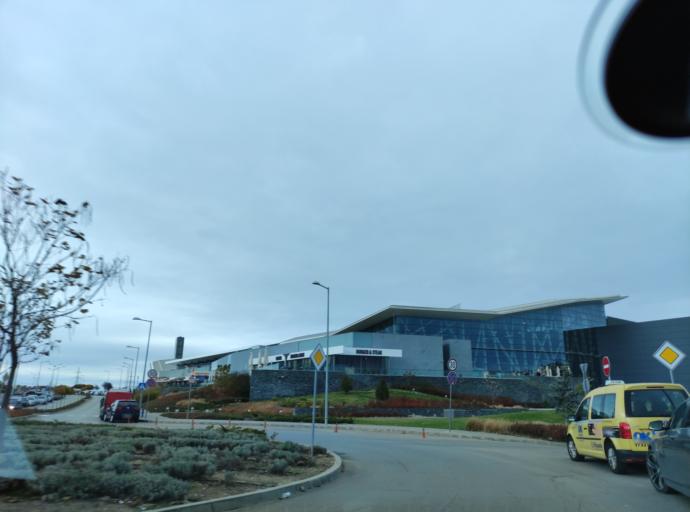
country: BG
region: Sofia-Capital
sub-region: Stolichna Obshtina
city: Sofia
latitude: 42.6228
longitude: 23.3539
